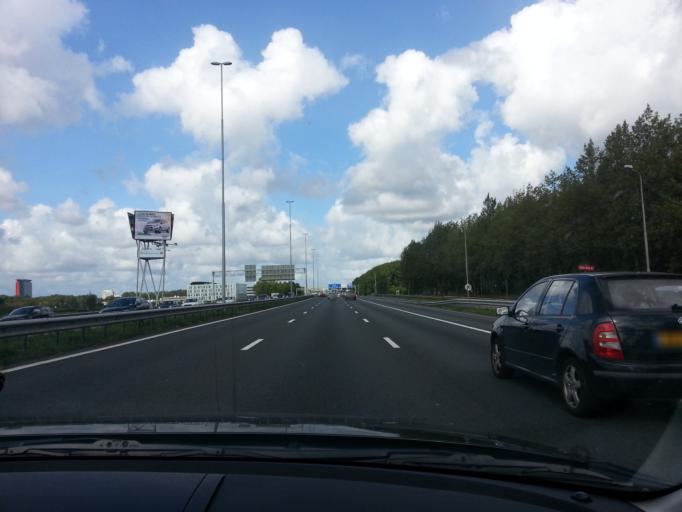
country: NL
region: South Holland
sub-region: Gemeente Delft
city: Delft
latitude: 51.9855
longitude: 4.3938
